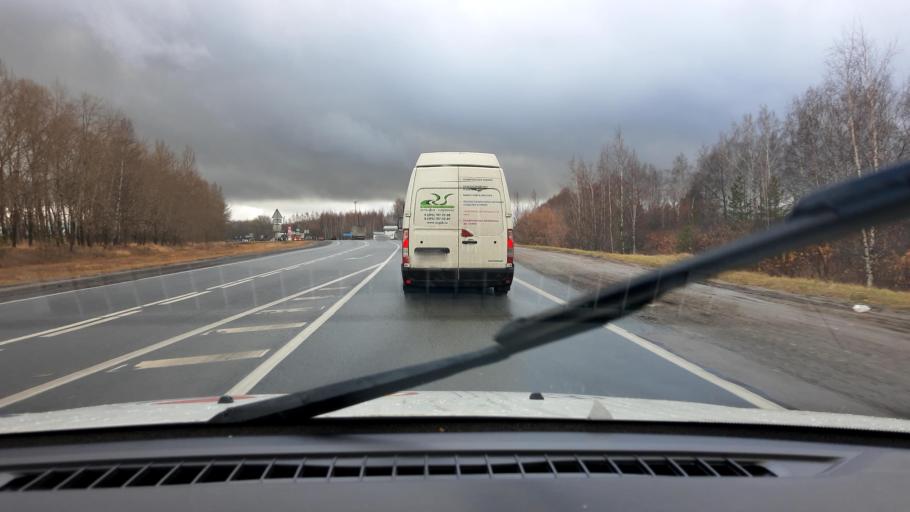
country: RU
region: Nizjnij Novgorod
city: Pamyat' Parizhskoy Kommuny
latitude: 56.0070
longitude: 44.6288
